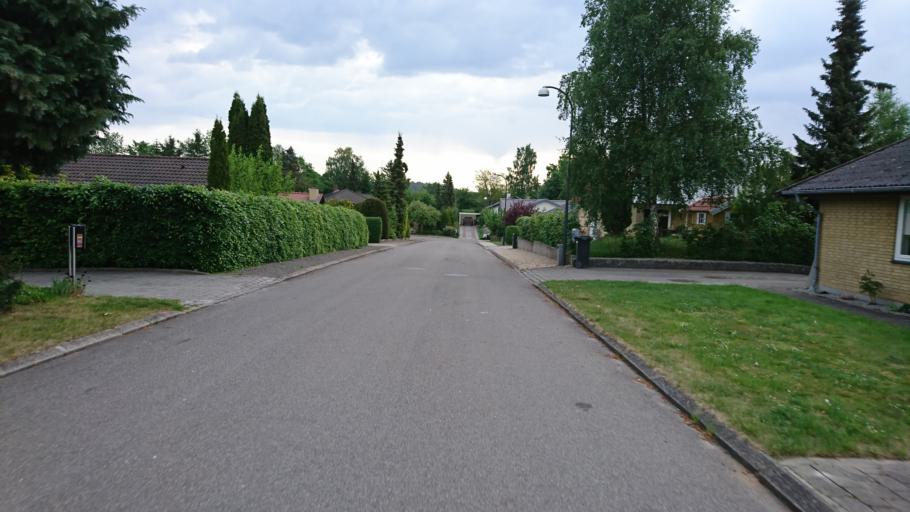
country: DK
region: Capital Region
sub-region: Fureso Kommune
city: Vaerlose
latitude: 55.7557
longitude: 12.3995
